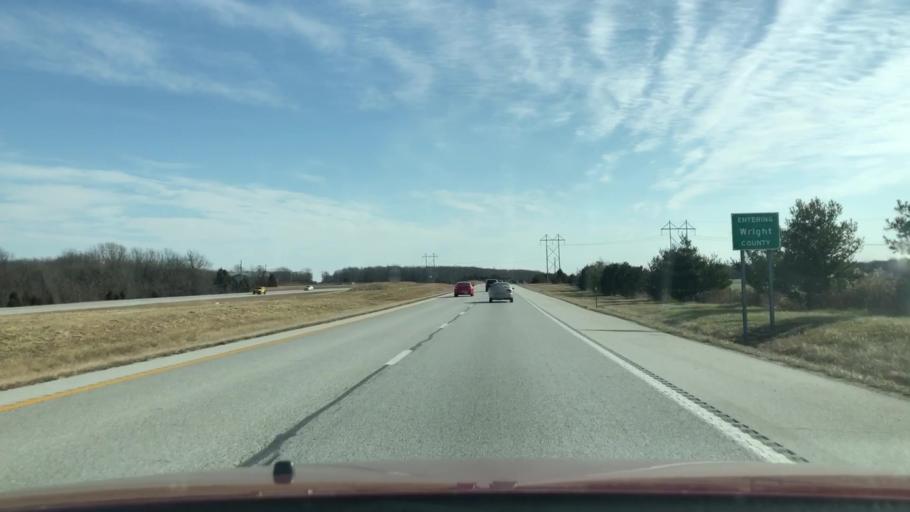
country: US
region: Missouri
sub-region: Webster County
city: Seymour
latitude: 37.1180
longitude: -92.6839
